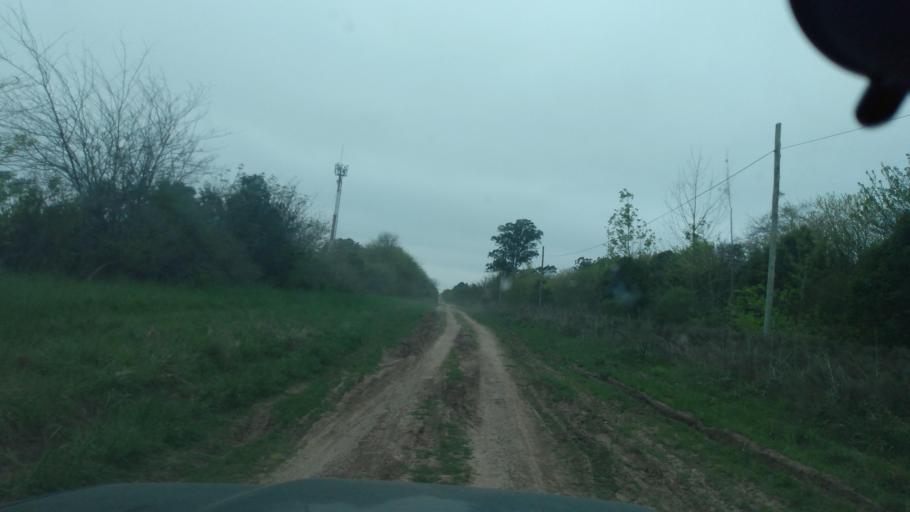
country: AR
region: Buenos Aires
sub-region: Partido de Lujan
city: Lujan
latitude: -34.5440
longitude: -59.2130
